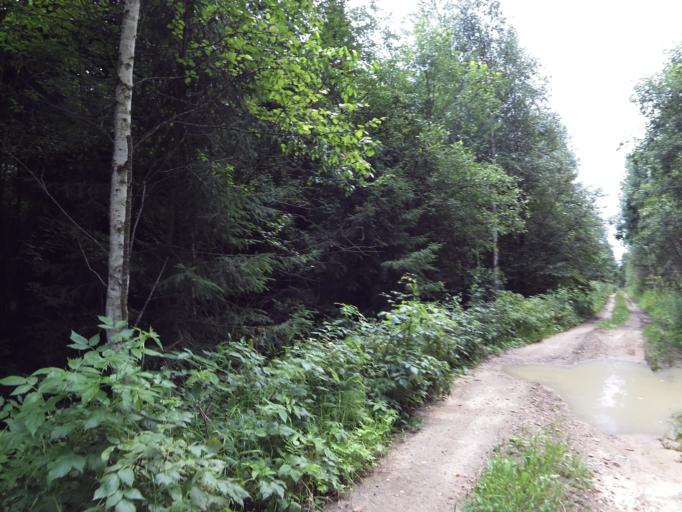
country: RU
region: Moskovskaya
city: Popovo
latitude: 54.9715
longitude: 37.6966
